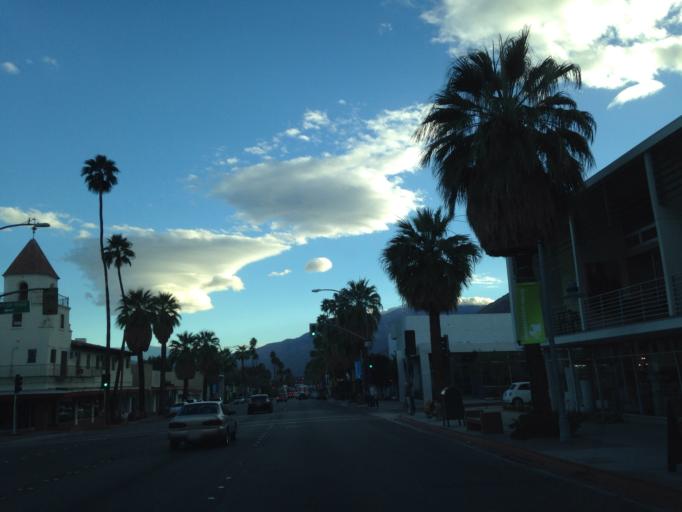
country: US
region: California
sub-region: Riverside County
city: Palm Springs
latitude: 33.8343
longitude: -116.5469
